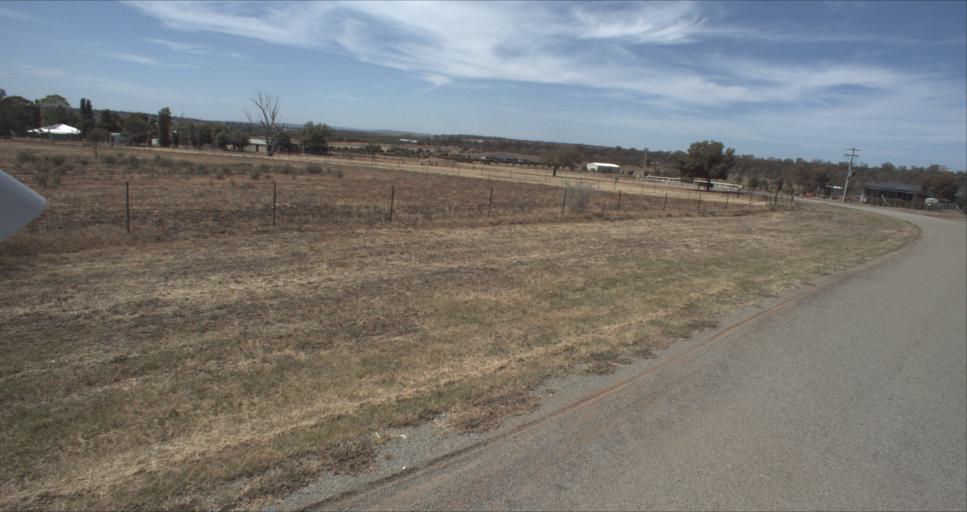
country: AU
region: New South Wales
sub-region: Leeton
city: Leeton
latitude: -34.5757
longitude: 146.4514
